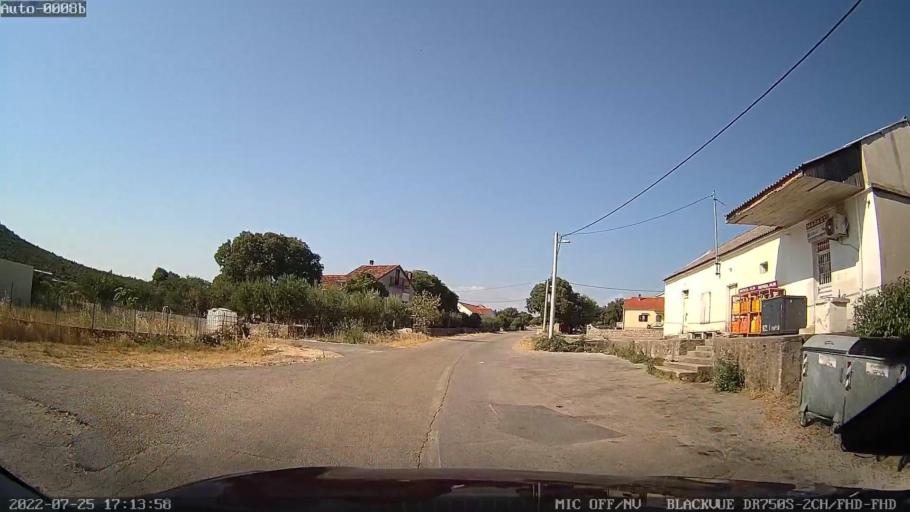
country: HR
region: Zadarska
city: Polaca
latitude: 44.0481
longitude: 15.5377
